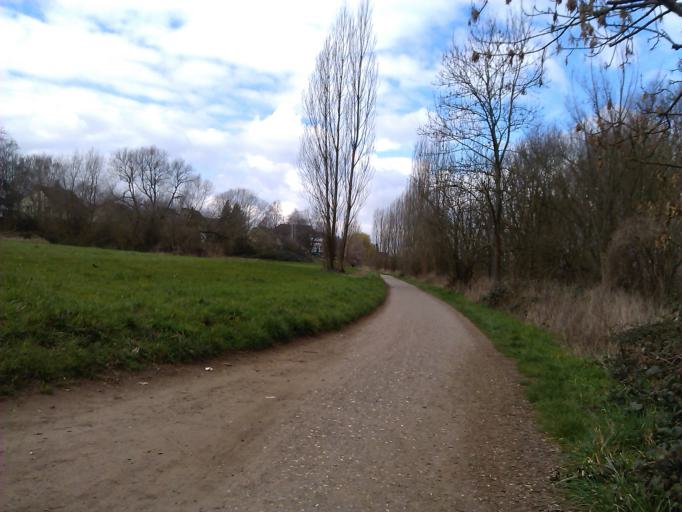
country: DE
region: Rheinland-Pfalz
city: Kaltenengers
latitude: 50.4154
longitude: 7.5538
